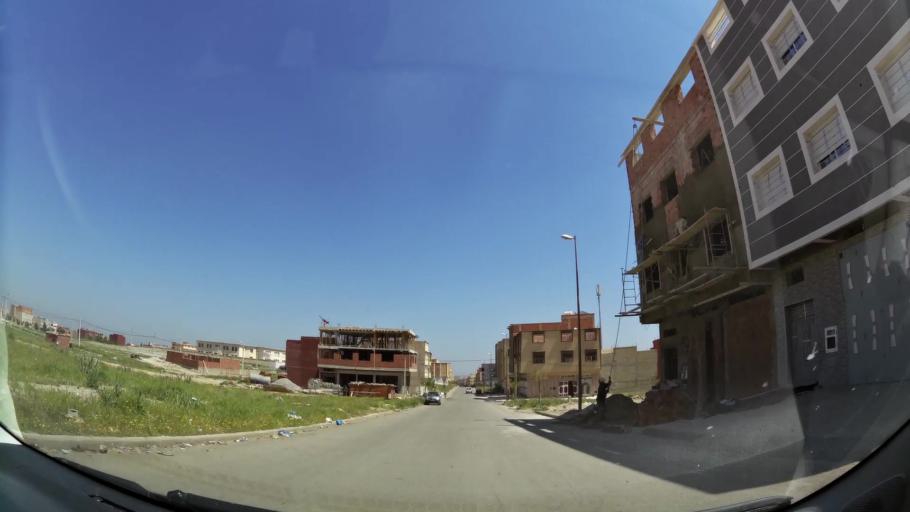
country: MA
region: Oriental
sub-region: Oujda-Angad
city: Oujda
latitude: 34.6778
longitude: -1.9444
